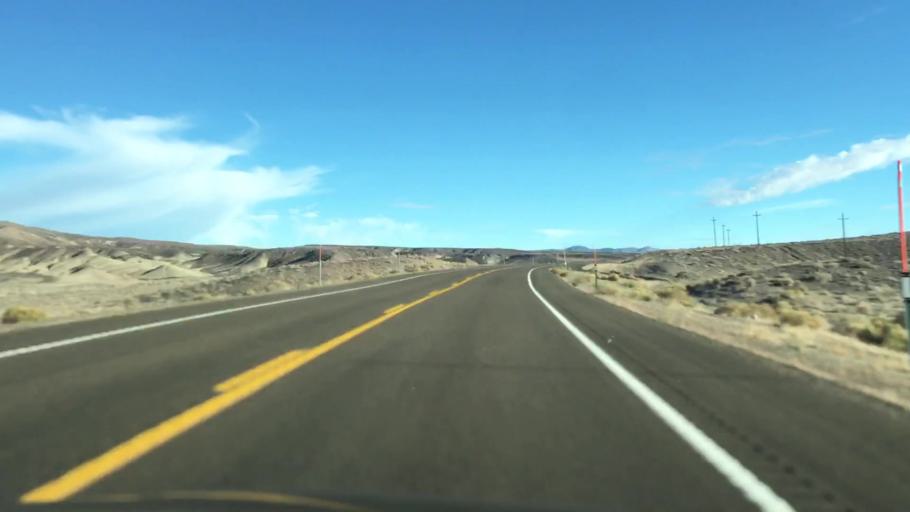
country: US
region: Nevada
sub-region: Mineral County
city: Hawthorne
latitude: 38.2360
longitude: -118.0275
